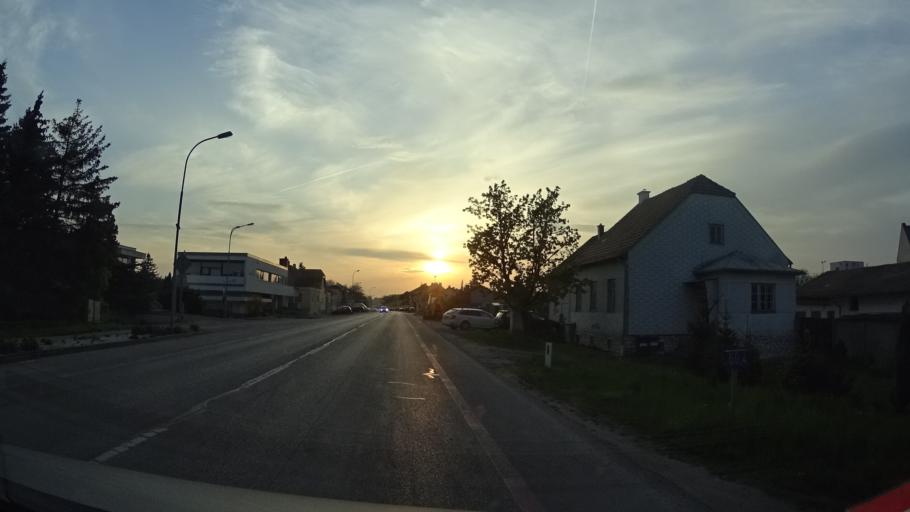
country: AT
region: Lower Austria
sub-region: Politischer Bezirk Korneuburg
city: Spillern
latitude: 48.3768
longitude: 16.2666
